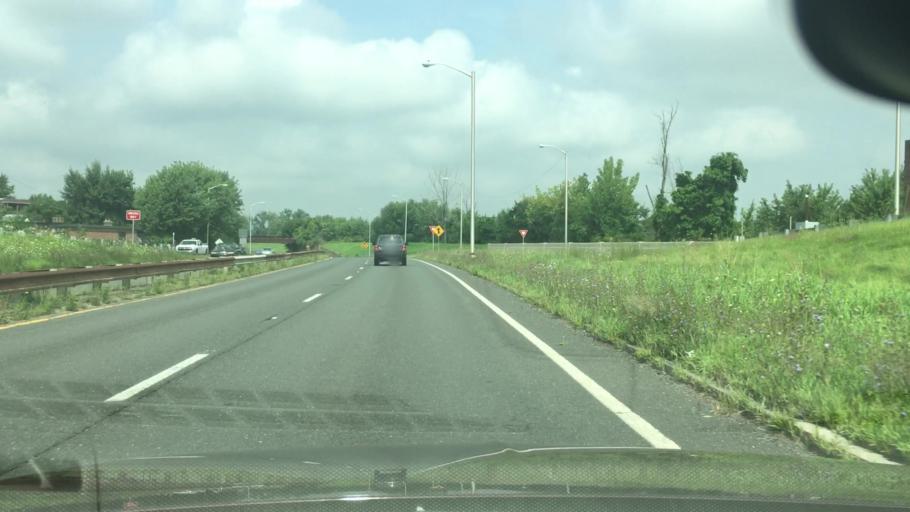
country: US
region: Massachusetts
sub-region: Hampden County
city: Springfield
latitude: 42.0985
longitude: -72.5981
